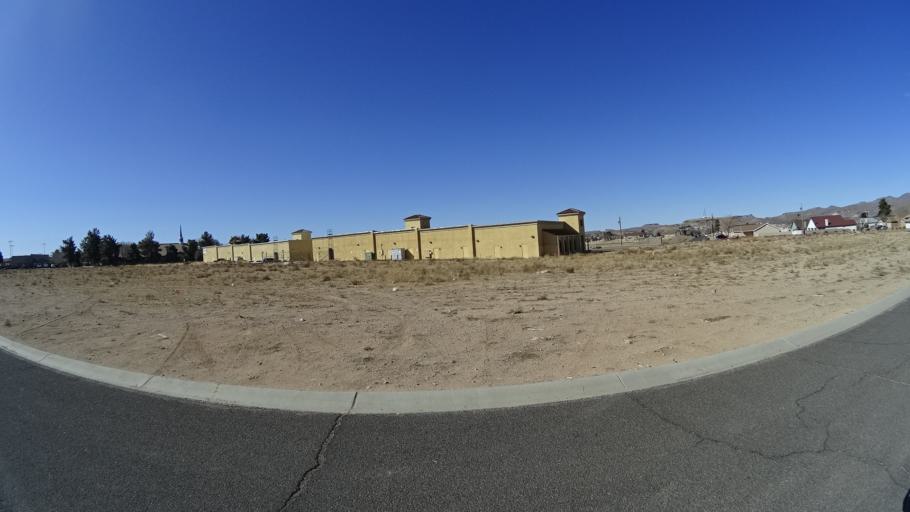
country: US
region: Arizona
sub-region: Mohave County
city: Kingman
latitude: 35.1973
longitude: -114.0098
